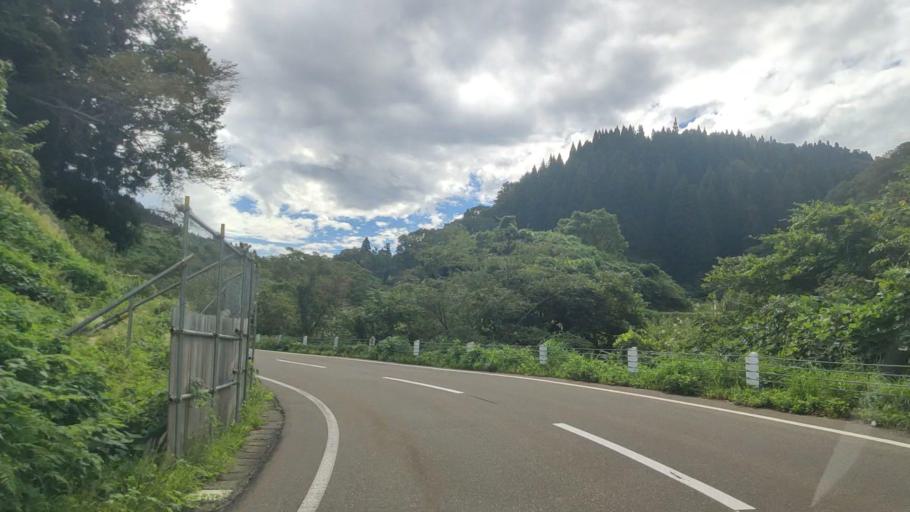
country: JP
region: Niigata
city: Arai
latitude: 36.9361
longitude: 138.2943
